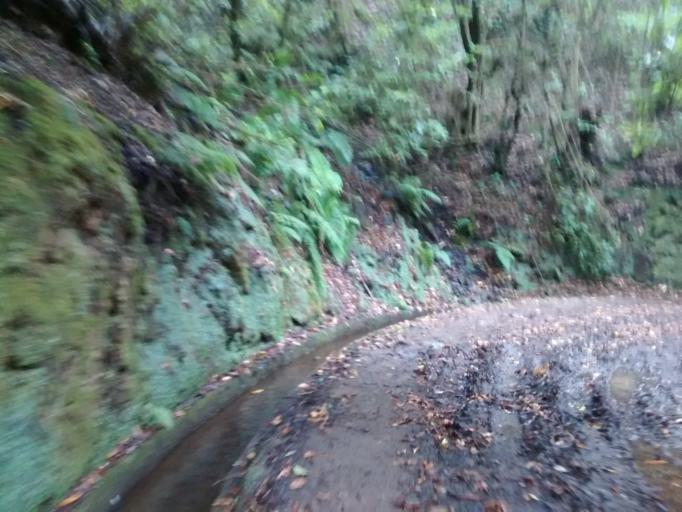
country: PT
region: Madeira
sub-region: Santana
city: Santana
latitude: 32.8069
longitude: -16.9377
